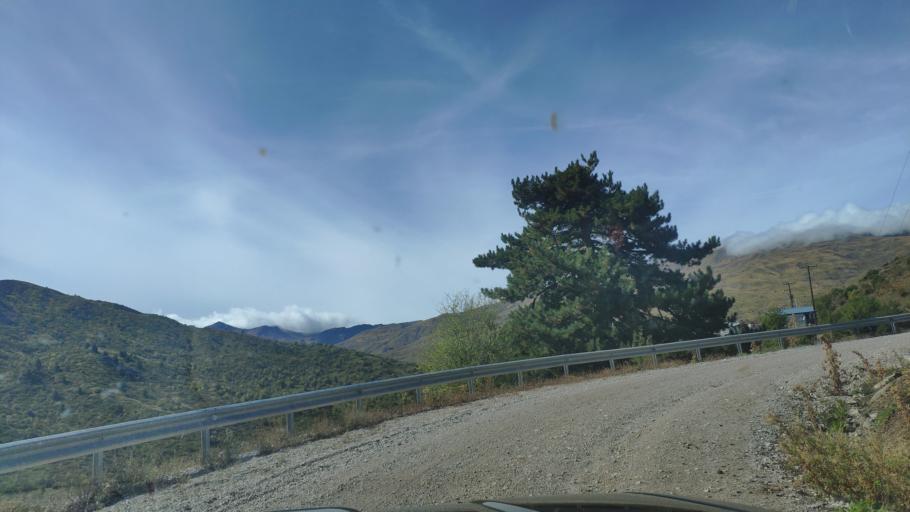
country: AL
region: Korce
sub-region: Rrethi i Devollit
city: Miras
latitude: 40.4013
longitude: 20.8504
